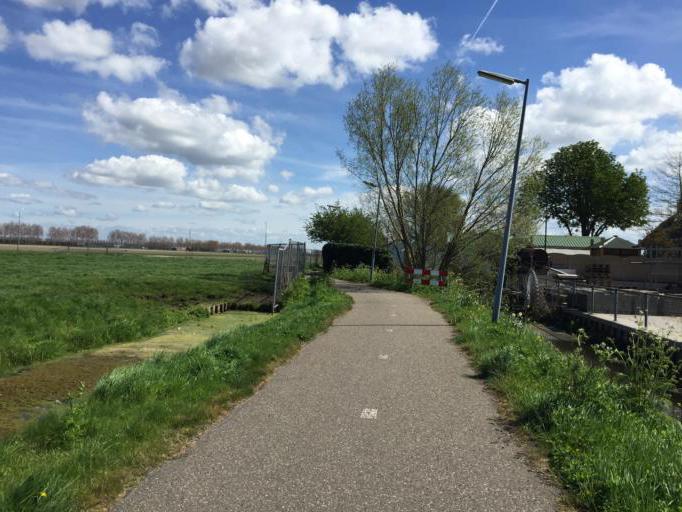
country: NL
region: South Holland
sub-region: Gemeente Lisse
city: Lisse
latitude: 52.2514
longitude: 4.5826
